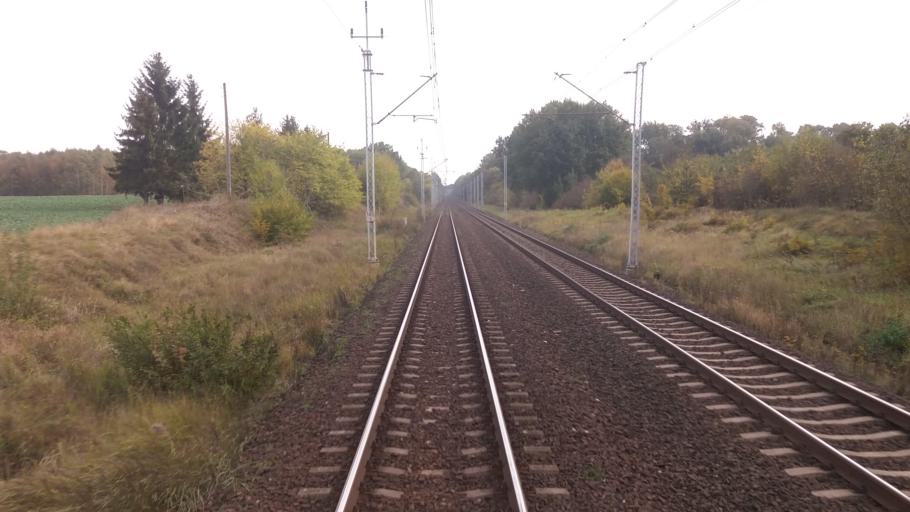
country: PL
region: West Pomeranian Voivodeship
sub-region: Powiat choszczenski
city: Choszczno
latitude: 53.1652
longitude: 15.3126
